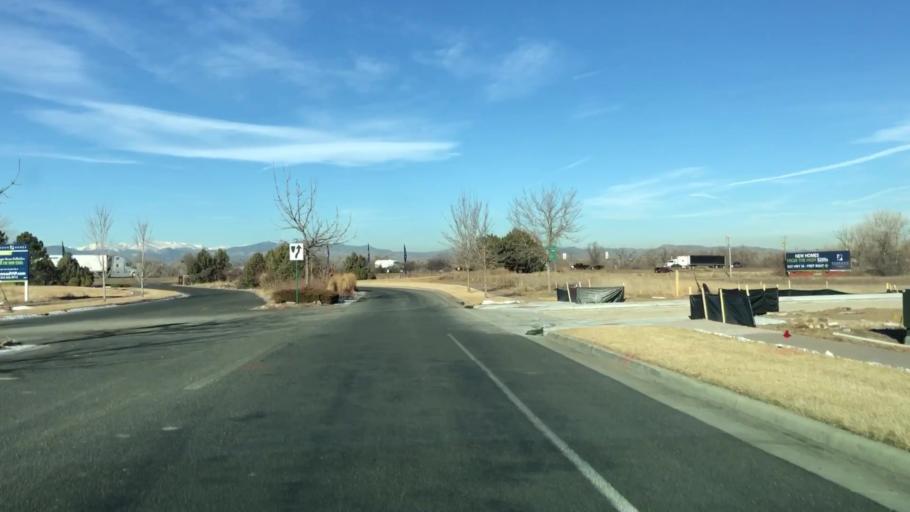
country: US
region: Colorado
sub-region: Larimer County
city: Loveland
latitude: 40.3911
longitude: -104.9914
